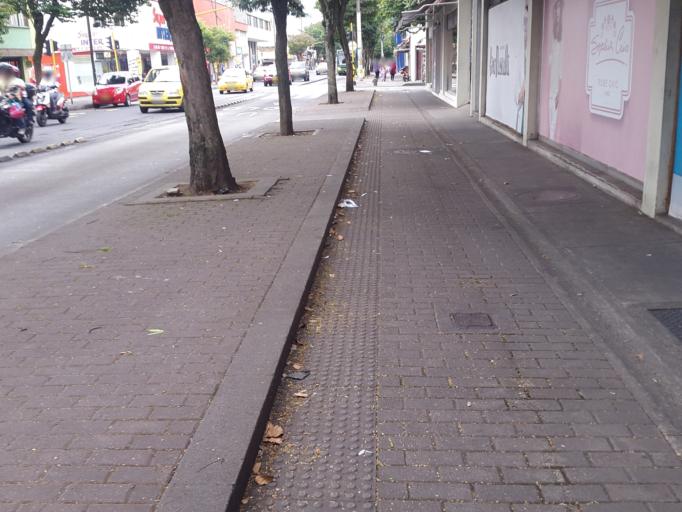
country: CO
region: Risaralda
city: Pereira
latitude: 4.8166
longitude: -75.7115
